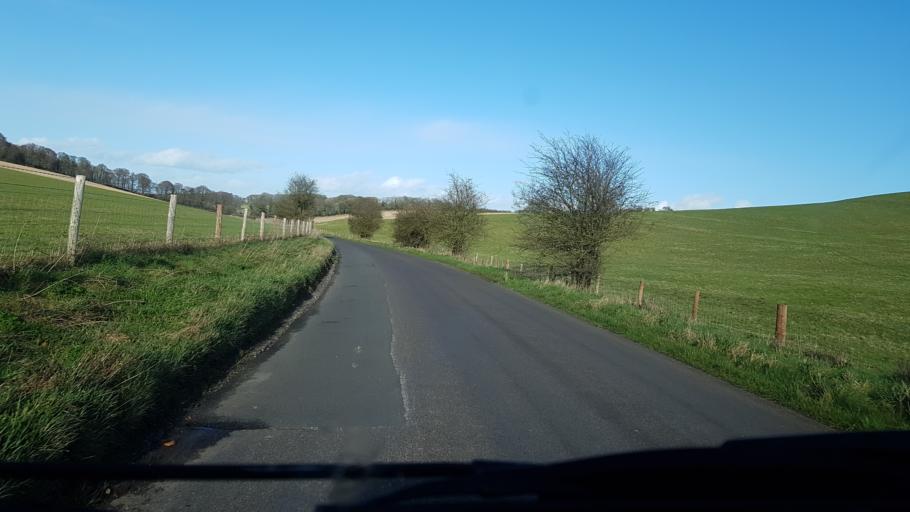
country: GB
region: England
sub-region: Wiltshire
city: Huish
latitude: 51.3793
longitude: -1.8247
